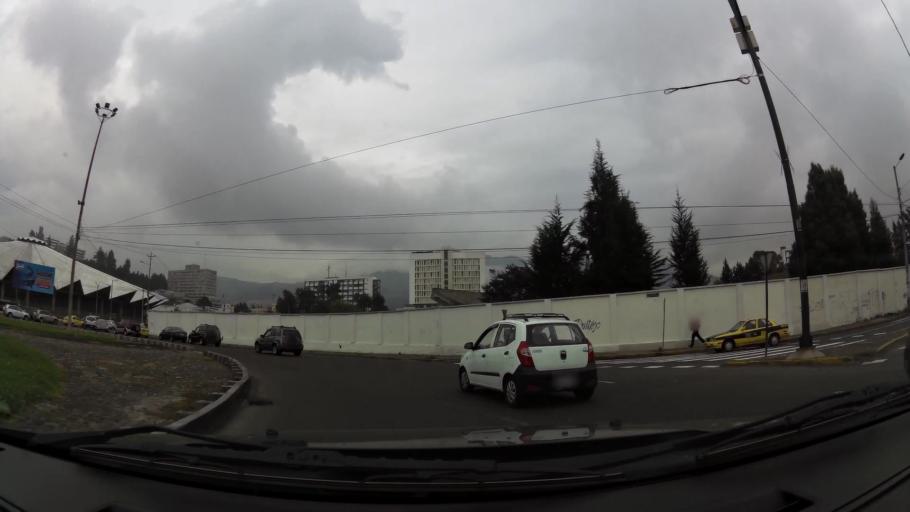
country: EC
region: Pichincha
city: Quito
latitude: -0.2125
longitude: -78.4886
